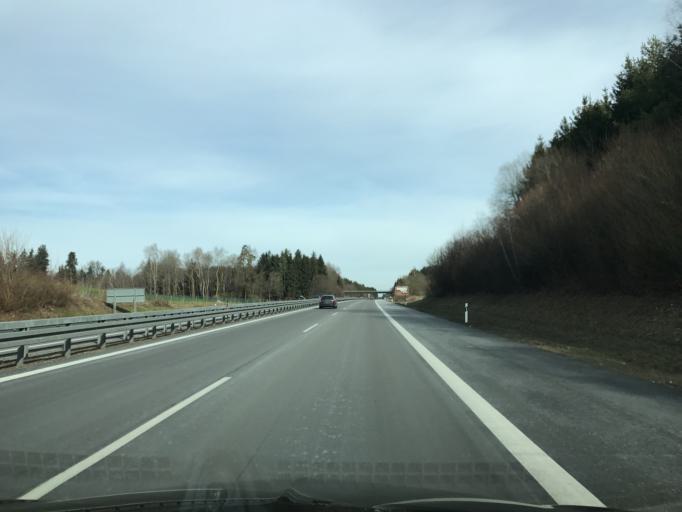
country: DE
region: Bavaria
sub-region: Swabia
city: Weissensberg
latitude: 47.6099
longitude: 9.7336
